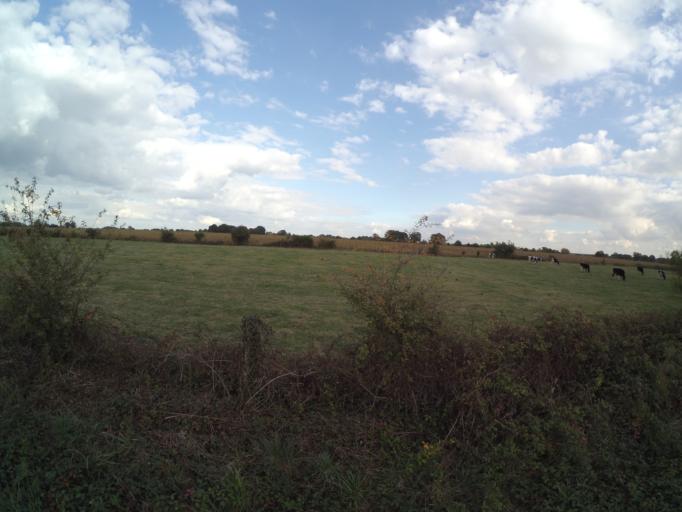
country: FR
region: Pays de la Loire
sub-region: Departement de la Loire-Atlantique
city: Saint-Lumine-de-Clisson
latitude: 47.0672
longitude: -1.3394
